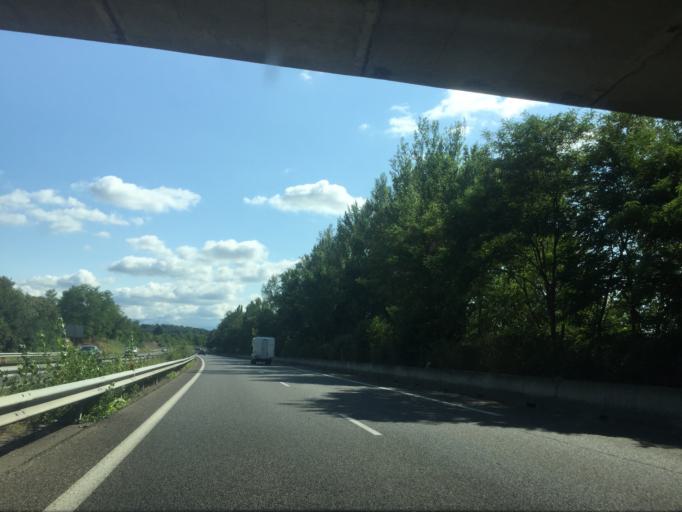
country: FR
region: Midi-Pyrenees
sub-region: Departement de la Haute-Garonne
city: Martres-Tolosane
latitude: 43.1704
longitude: 0.9732
